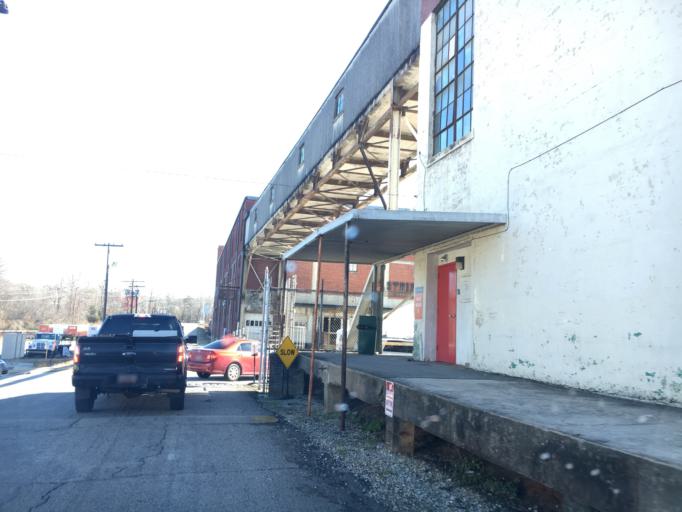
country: US
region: South Carolina
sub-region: Greenville County
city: Taylors
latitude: 34.9200
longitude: -82.2852
